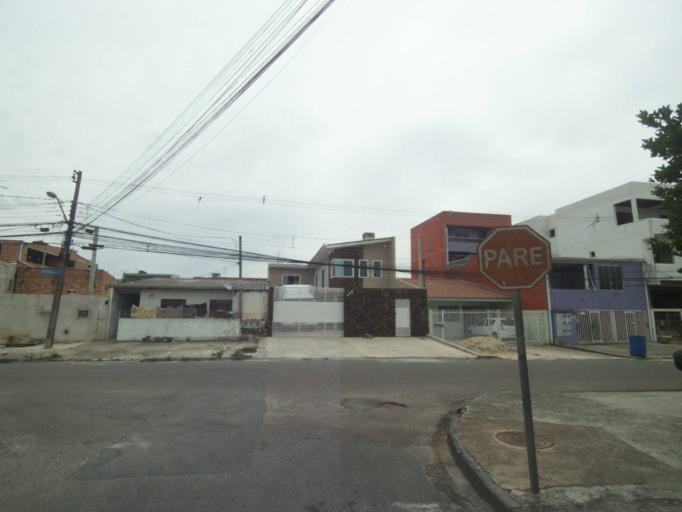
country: BR
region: Parana
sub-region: Curitiba
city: Curitiba
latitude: -25.5121
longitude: -49.3362
